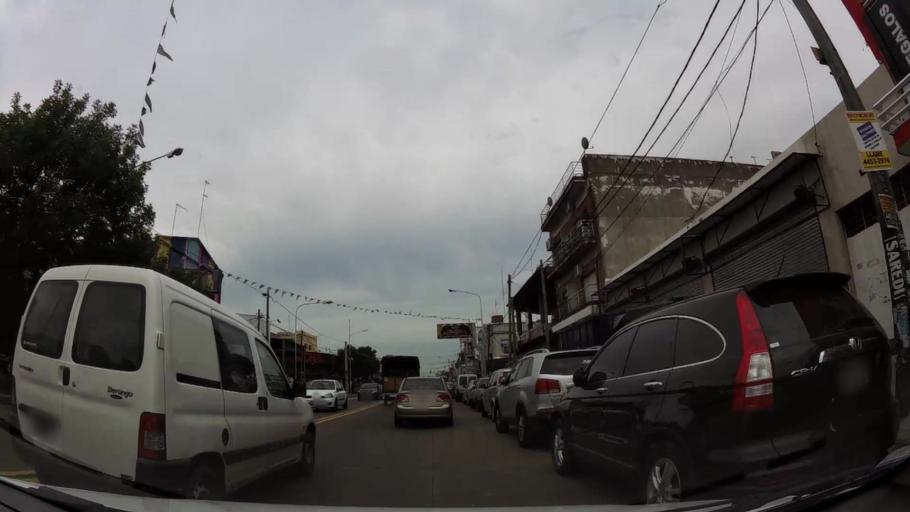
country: AR
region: Buenos Aires F.D.
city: Villa Lugano
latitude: -34.6791
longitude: -58.5098
